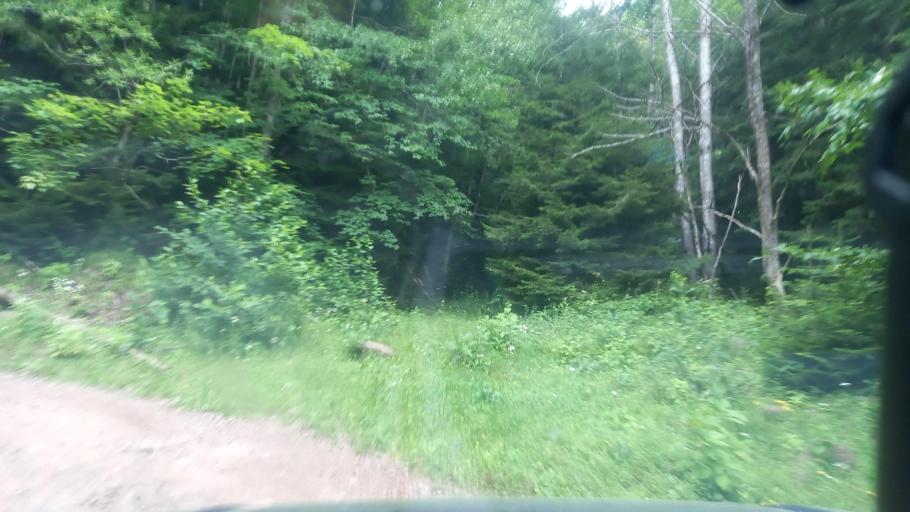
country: RU
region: Karachayevo-Cherkesiya
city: Kurdzhinovo
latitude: 43.8151
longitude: 40.8794
